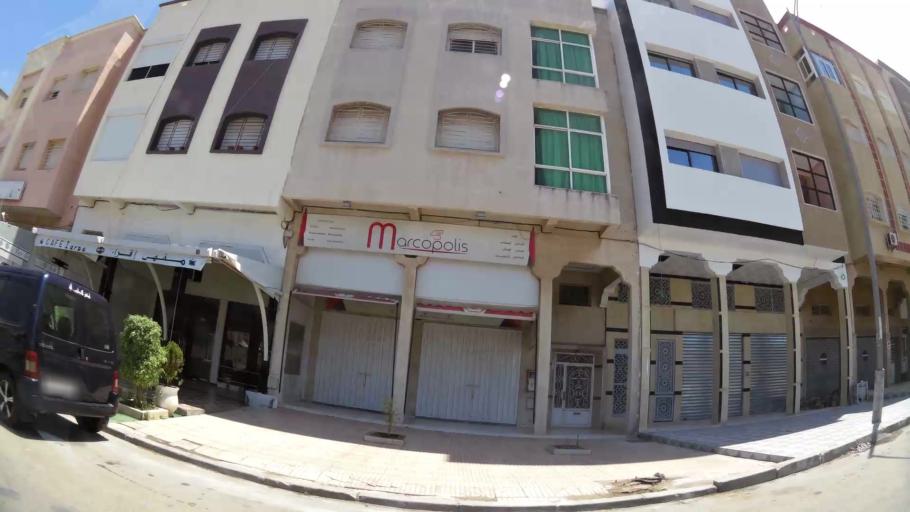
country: MA
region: Gharb-Chrarda-Beni Hssen
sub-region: Kenitra Province
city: Kenitra
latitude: 34.2559
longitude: -6.6153
